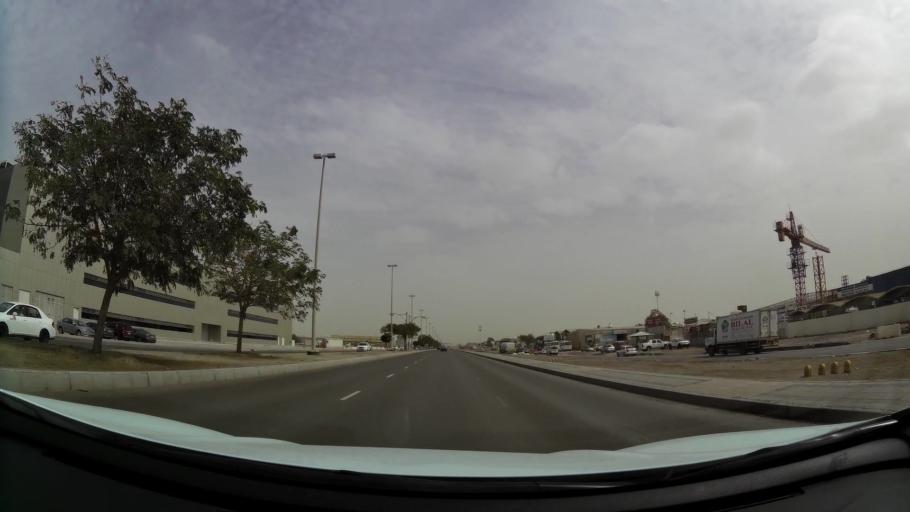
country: AE
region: Abu Dhabi
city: Abu Dhabi
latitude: 24.3590
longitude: 54.4963
